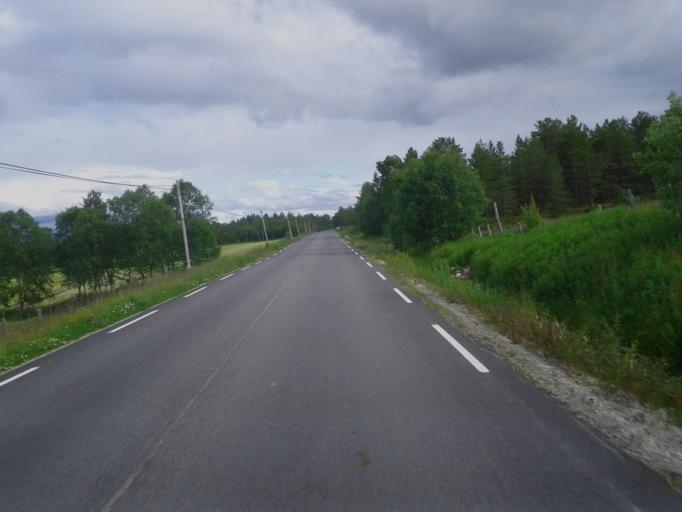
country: NO
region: Sor-Trondelag
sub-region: Roros
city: Roros
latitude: 62.3004
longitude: 11.7215
